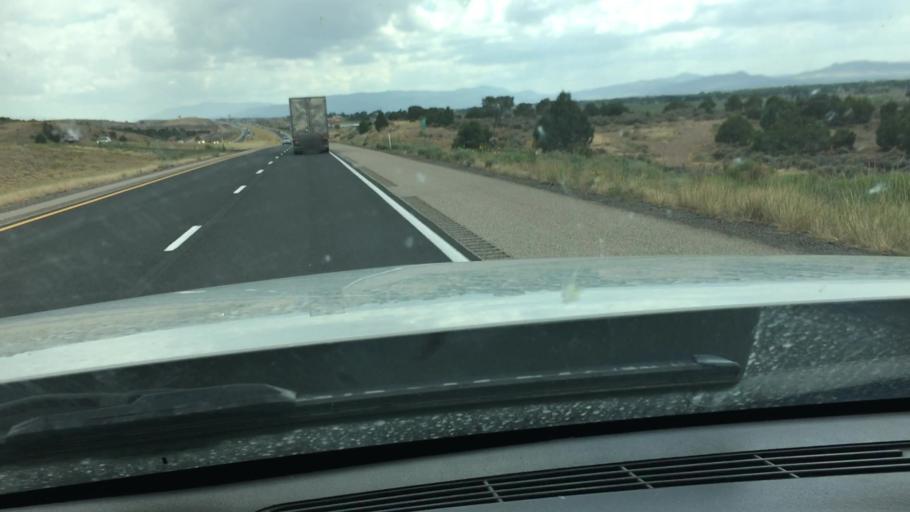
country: US
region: Utah
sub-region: Iron County
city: Enoch
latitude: 37.7568
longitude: -113.0229
